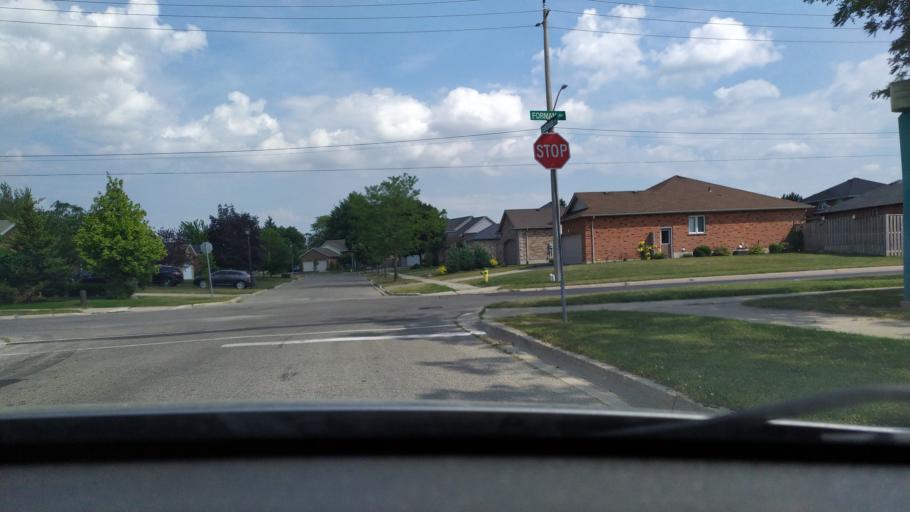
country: CA
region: Ontario
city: Stratford
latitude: 43.3837
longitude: -80.9939
